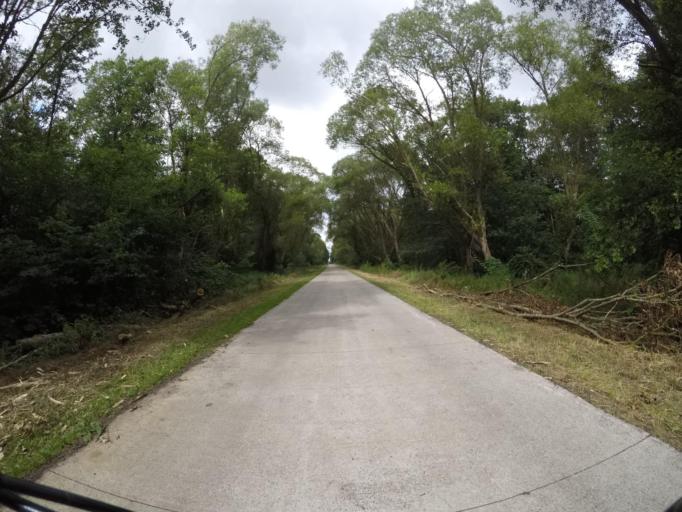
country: DE
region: Lower Saxony
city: Damnatz
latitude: 53.1929
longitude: 11.1258
